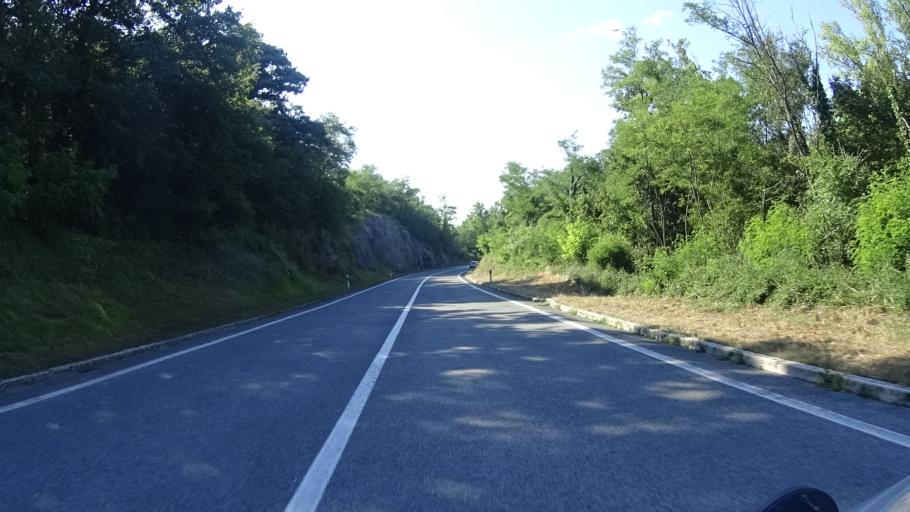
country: HR
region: Istarska
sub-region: Grad Labin
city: Labin
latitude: 45.1877
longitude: 14.1353
